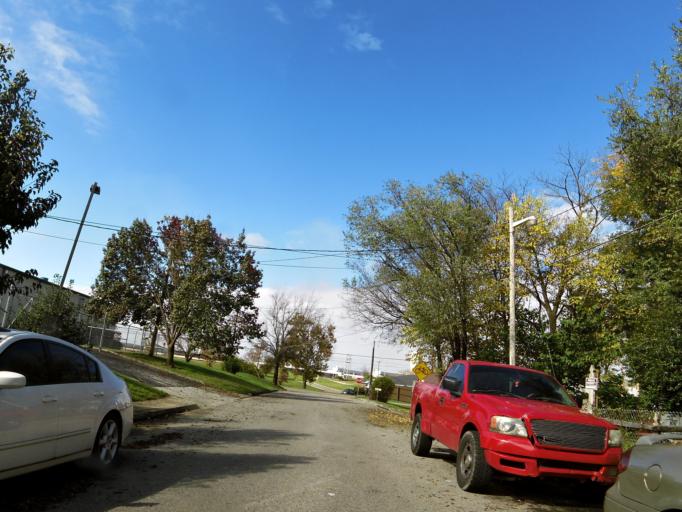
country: US
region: Tennessee
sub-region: Blount County
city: Maryville
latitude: 35.7701
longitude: -83.9660
